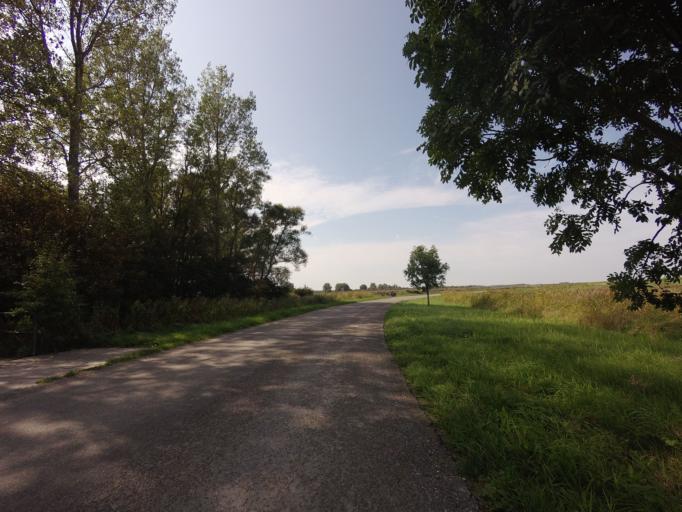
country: NL
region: Groningen
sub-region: Gemeente De Marne
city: Ulrum
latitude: 53.3408
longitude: 6.2921
